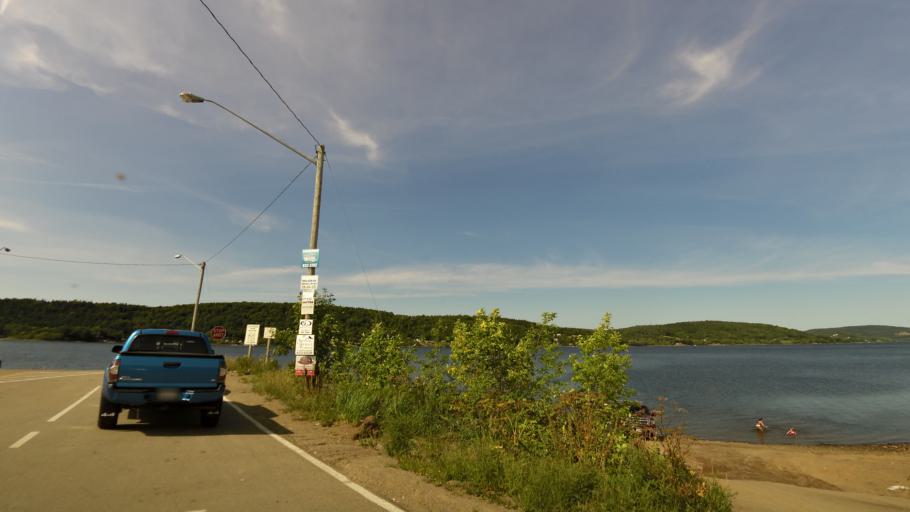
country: CA
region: New Brunswick
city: Hampton
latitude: 45.6105
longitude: -65.9017
